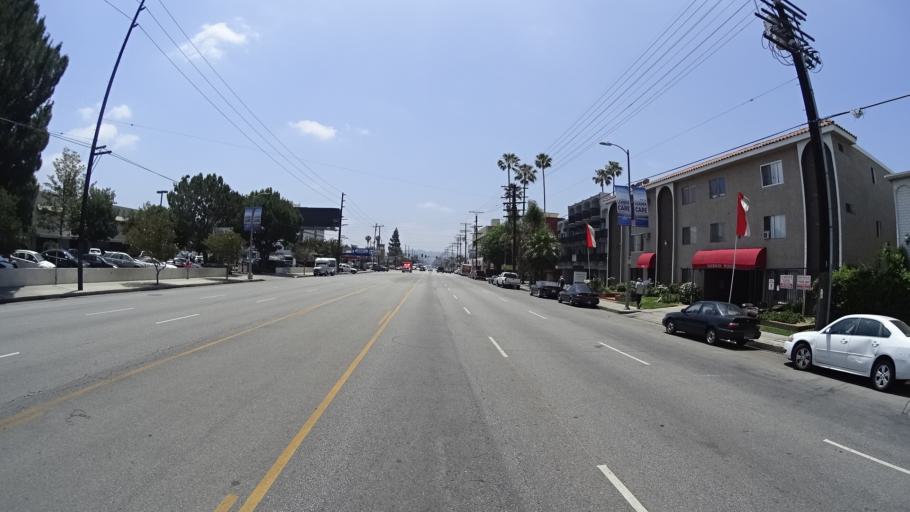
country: US
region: California
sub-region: Los Angeles County
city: Van Nuys
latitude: 34.1957
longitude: -118.4663
